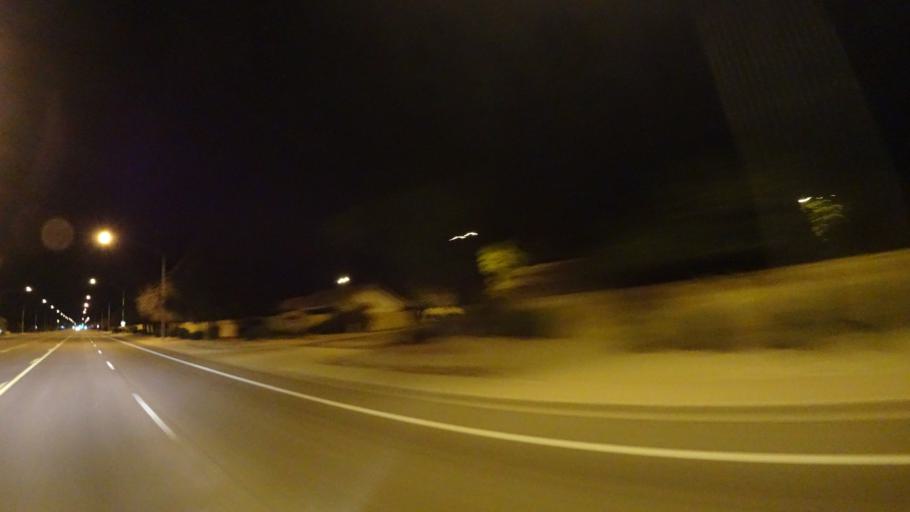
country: US
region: Arizona
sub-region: Maricopa County
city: Mesa
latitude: 33.4396
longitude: -111.7189
